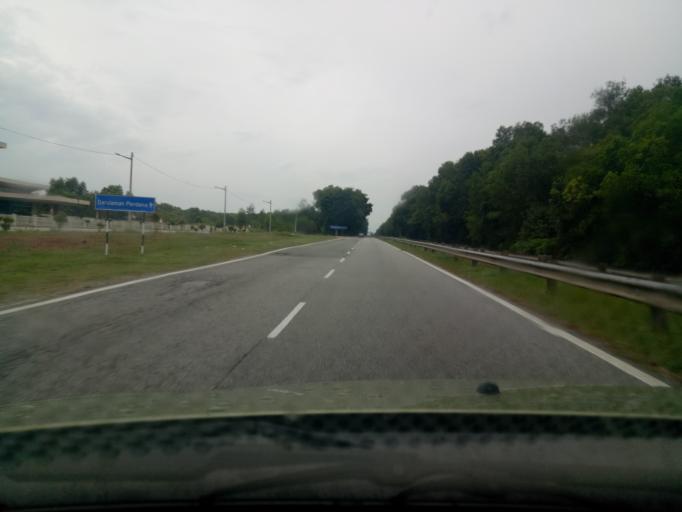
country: MY
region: Kedah
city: Sungai Petani
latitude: 5.6679
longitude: 100.5205
